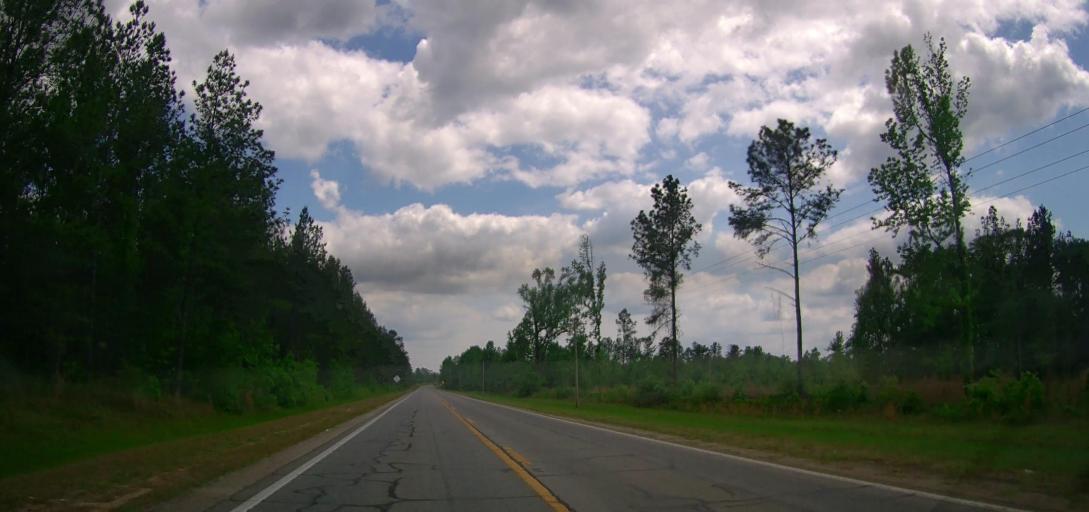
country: US
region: Georgia
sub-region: Laurens County
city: East Dublin
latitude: 32.4898
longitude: -82.8257
